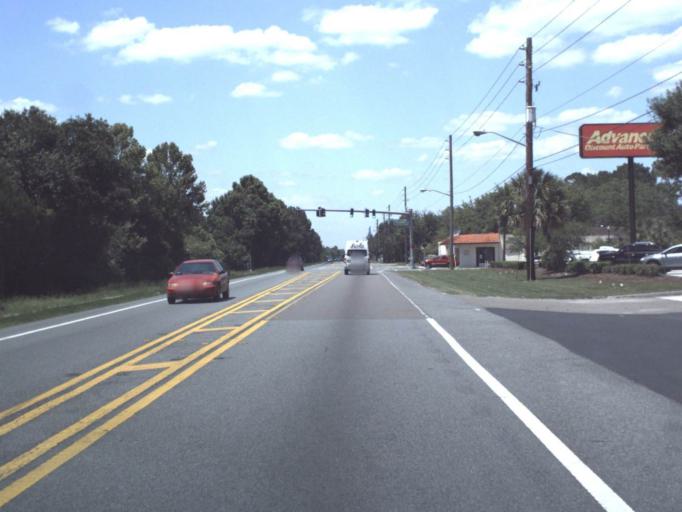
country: US
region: Florida
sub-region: Duval County
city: Jacksonville
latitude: 30.4660
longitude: -81.6331
